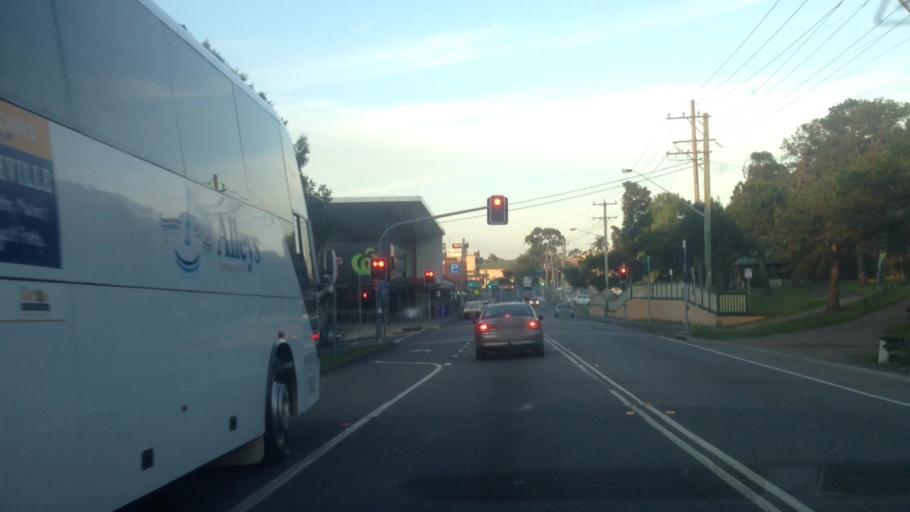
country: AU
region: New South Wales
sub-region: Lake Macquarie Shire
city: Dora Creek
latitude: -33.1100
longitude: 151.4855
